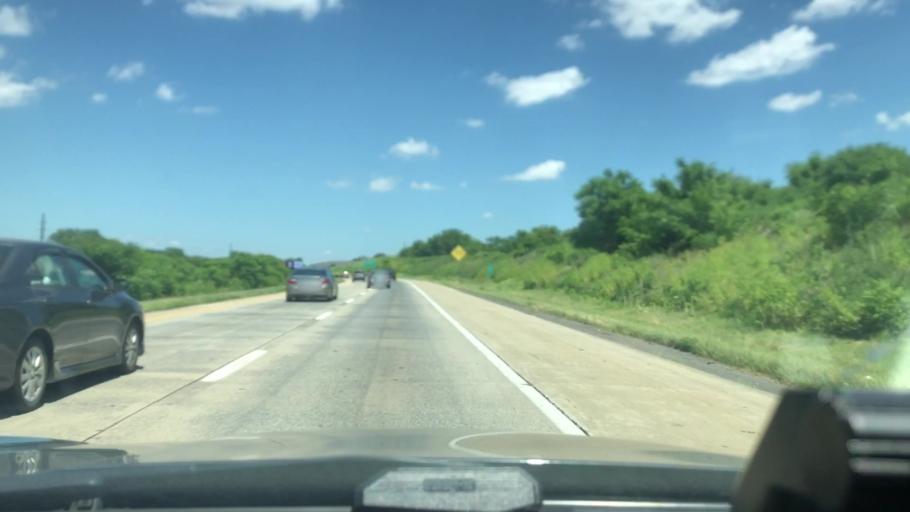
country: US
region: Pennsylvania
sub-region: Lehigh County
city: Ancient Oaks
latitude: 40.5877
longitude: -75.5928
